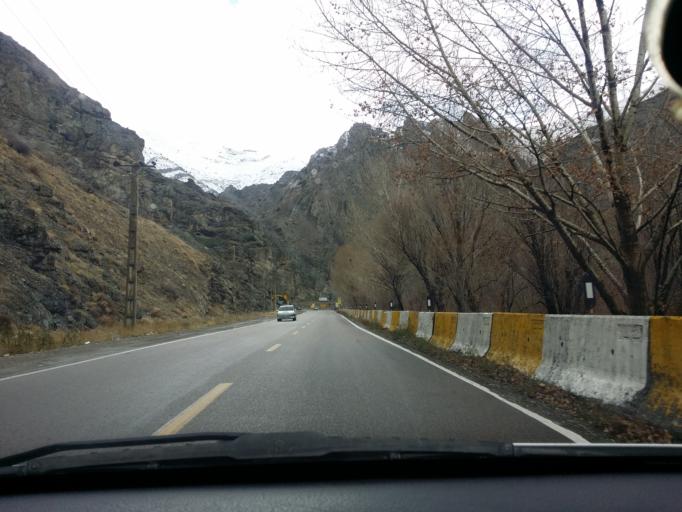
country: IR
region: Tehran
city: Tajrish
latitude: 36.0143
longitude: 51.2876
